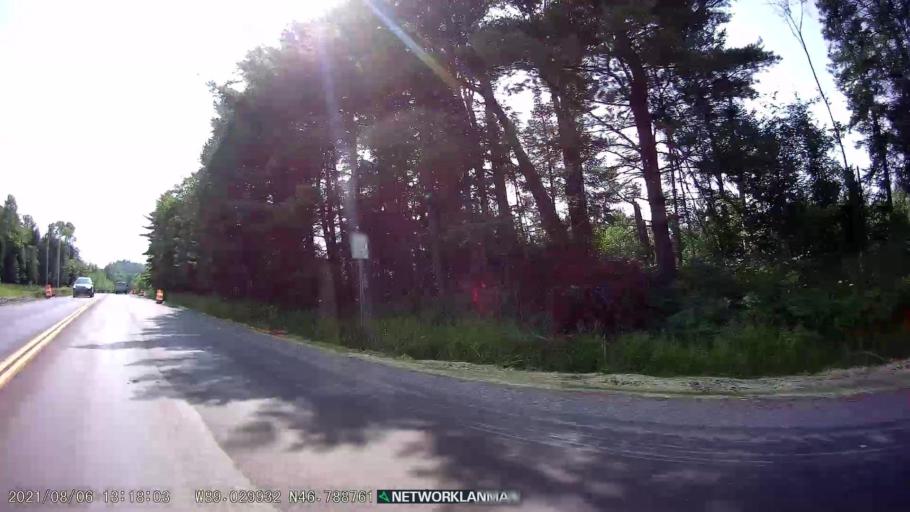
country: US
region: Michigan
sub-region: Ontonagon County
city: Ontonagon
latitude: 46.7887
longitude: -89.0300
